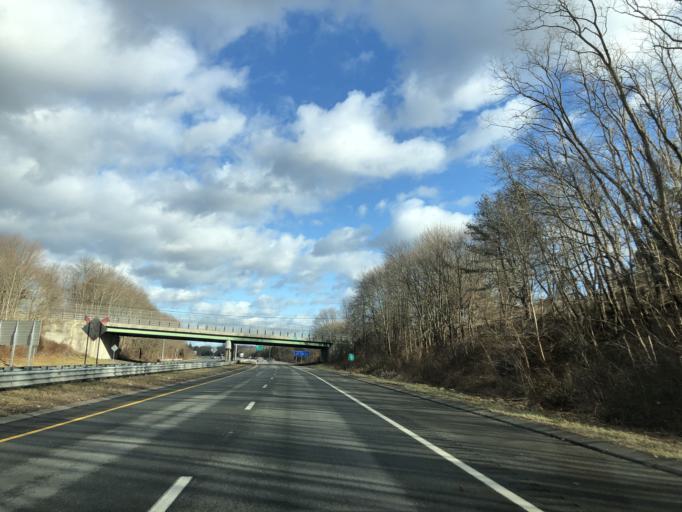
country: US
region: Massachusetts
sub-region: Bristol County
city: Fairhaven
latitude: 41.6539
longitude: -70.9085
